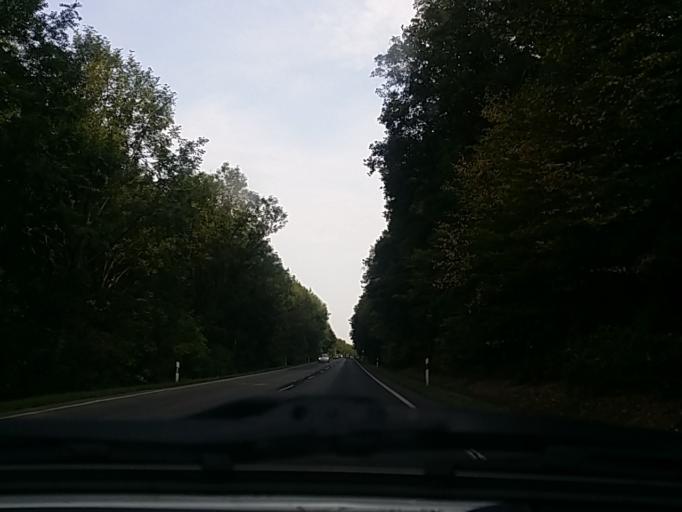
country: HU
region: Fejer
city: Szarliget
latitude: 47.5114
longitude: 18.4823
